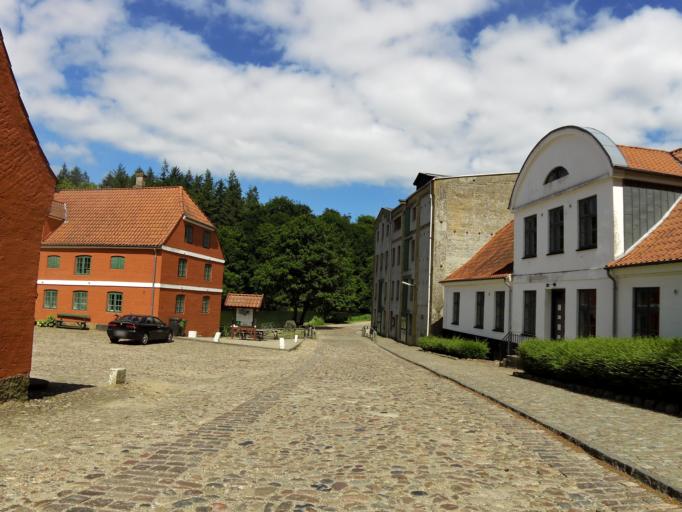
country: DK
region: South Denmark
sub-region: Haderslev Kommune
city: Vojens
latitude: 55.2376
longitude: 9.3735
